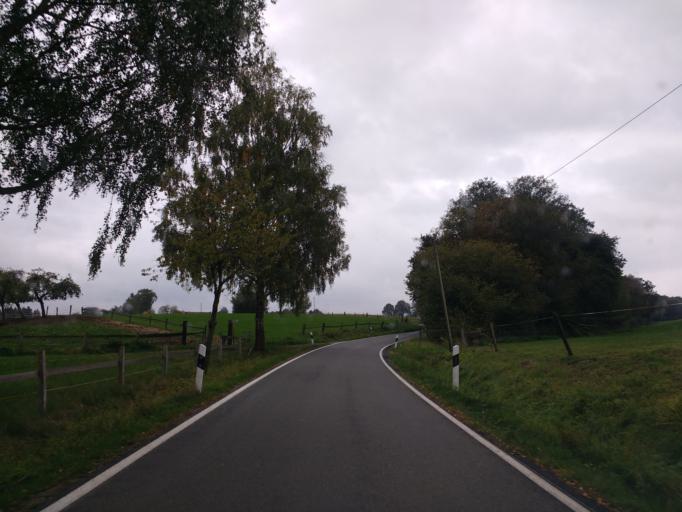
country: DE
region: North Rhine-Westphalia
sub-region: Regierungsbezirk Detmold
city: Dorentrup
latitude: 51.9904
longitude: 8.9589
